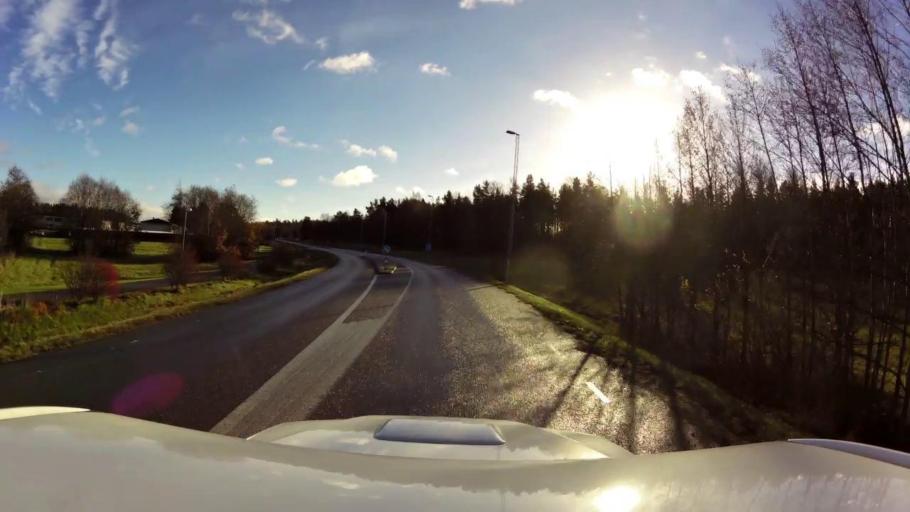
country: SE
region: OEstergoetland
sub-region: Linkopings Kommun
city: Linkoping
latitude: 58.3768
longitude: 15.6368
